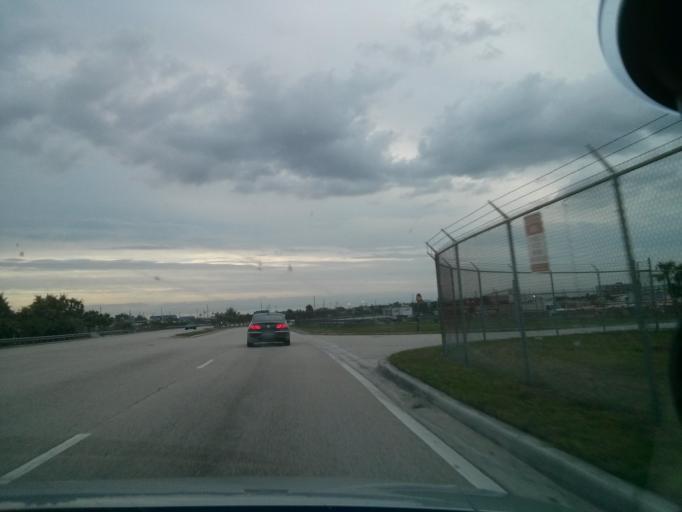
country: US
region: Florida
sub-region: Miami-Dade County
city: Virginia Gardens
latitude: 25.7986
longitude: -80.3065
